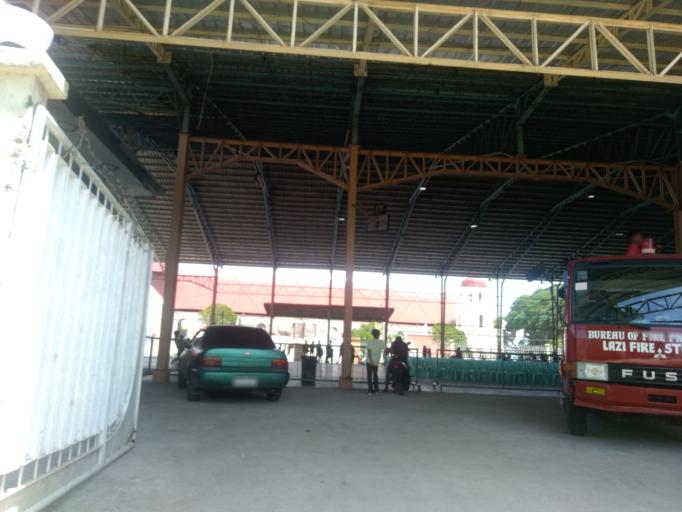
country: PH
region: Central Visayas
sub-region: Province of Siquijor
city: Lazi
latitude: 9.1286
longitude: 123.6334
